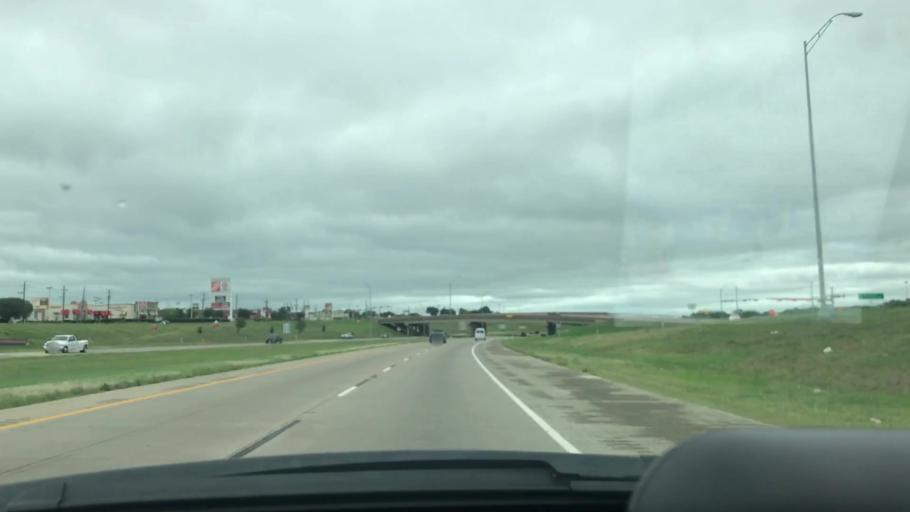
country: US
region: Texas
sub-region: Grayson County
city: Sherman
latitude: 33.6780
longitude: -96.6086
